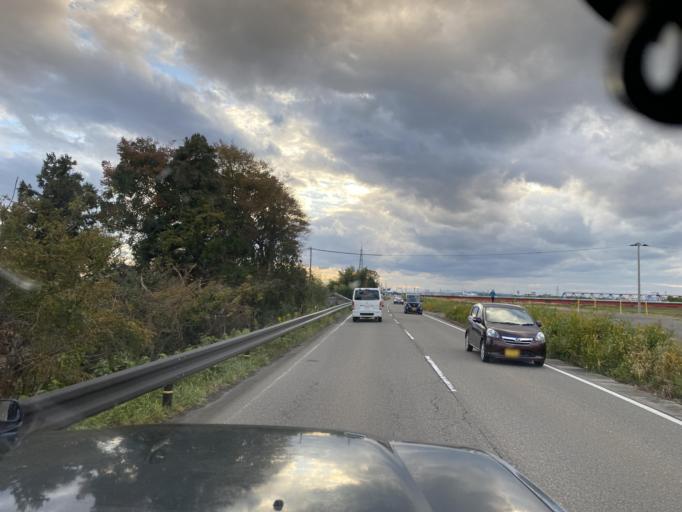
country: JP
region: Niigata
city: Sanjo
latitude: 37.6468
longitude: 138.9532
